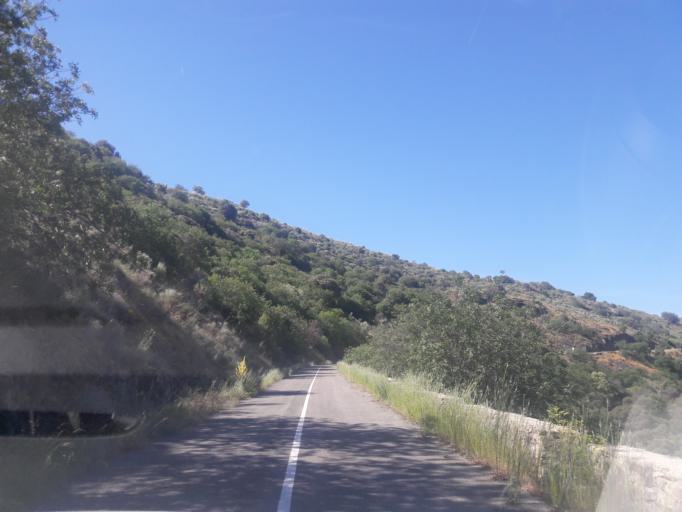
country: ES
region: Castille and Leon
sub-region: Provincia de Salamanca
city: Saucelle
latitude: 41.0232
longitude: -6.7489
